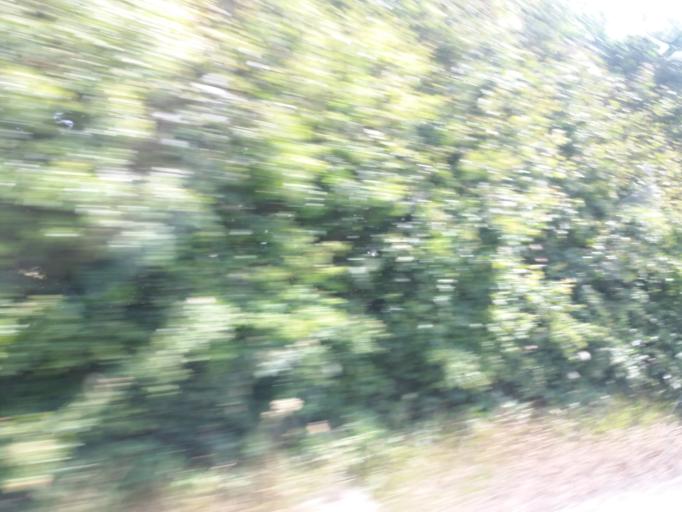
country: IE
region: Leinster
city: Balrothery
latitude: 53.5464
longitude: -6.2060
